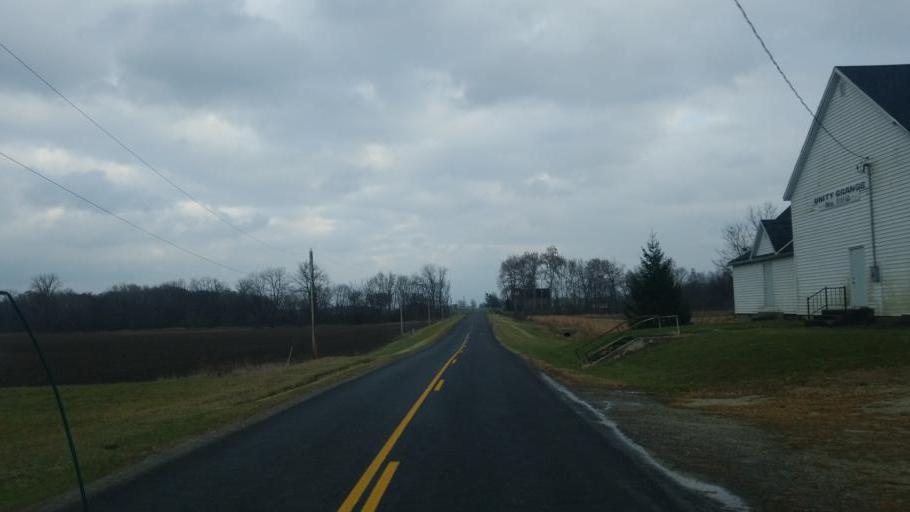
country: US
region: Ohio
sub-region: Mercer County
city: Fort Recovery
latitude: 40.5090
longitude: -84.7467
